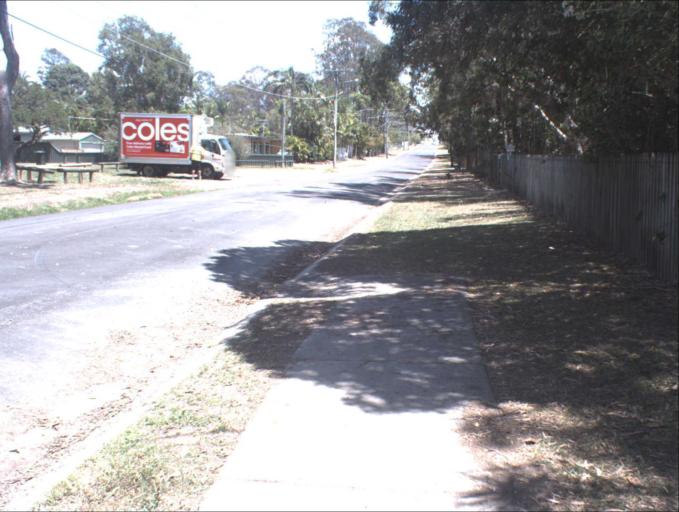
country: AU
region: Queensland
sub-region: Logan
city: Beenleigh
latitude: -27.7002
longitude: 153.2076
